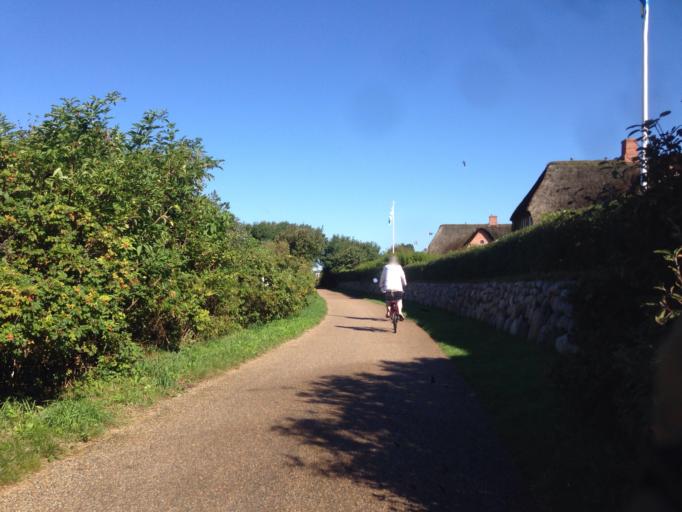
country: DE
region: Schleswig-Holstein
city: Tinnum
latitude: 54.9485
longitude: 8.3361
